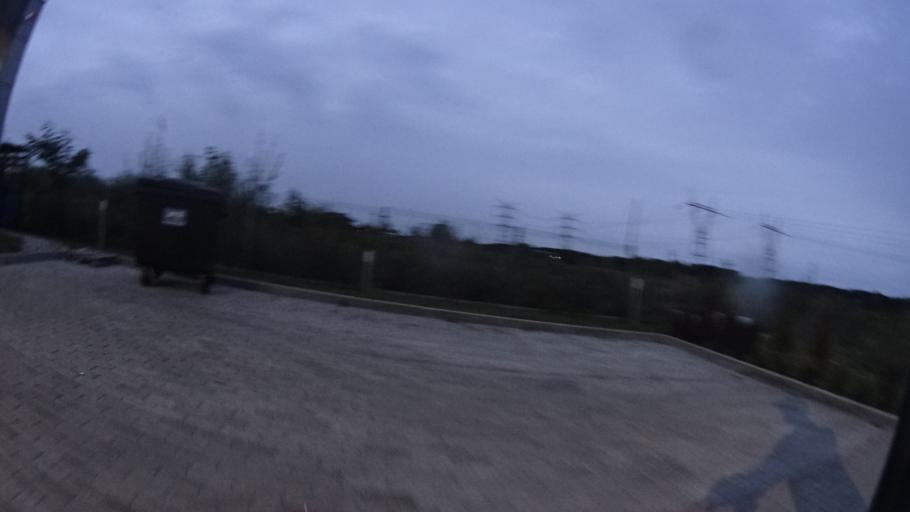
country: PL
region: Masovian Voivodeship
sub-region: Powiat warszawski zachodni
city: Lomianki
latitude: 52.2891
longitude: 20.8763
